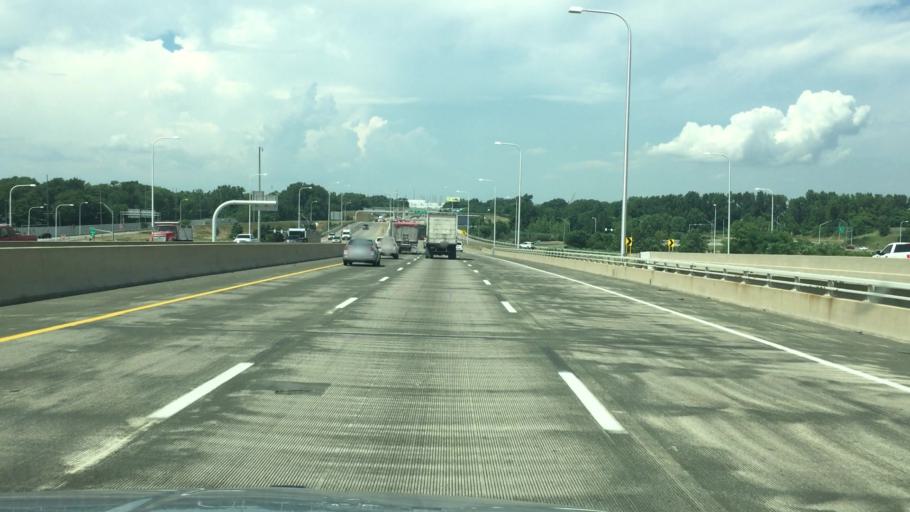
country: US
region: Ohio
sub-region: Lucas County
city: Oregon
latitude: 41.6721
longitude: -83.5149
